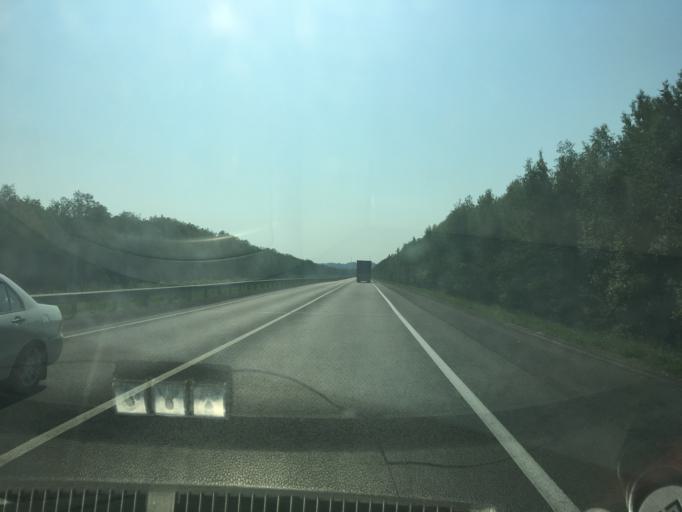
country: RU
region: Nizjnij Novgorod
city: Pamyat' Parizhskoy Kommuny
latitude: 56.0842
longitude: 44.3504
